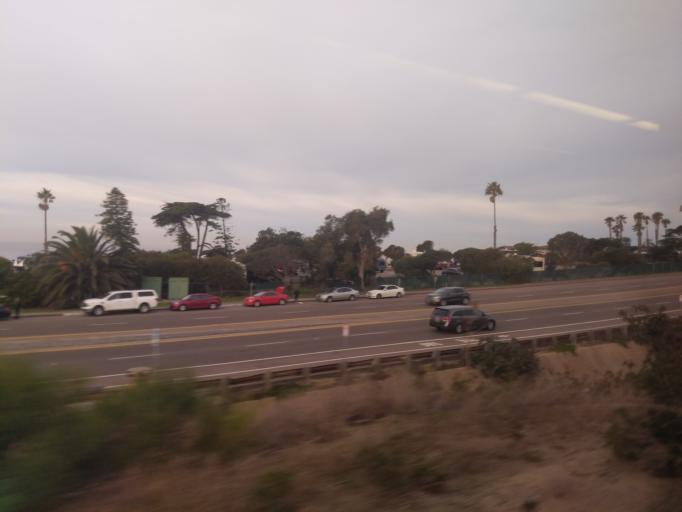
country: US
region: California
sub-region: San Diego County
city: Encinitas
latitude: 33.0203
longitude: -117.2826
